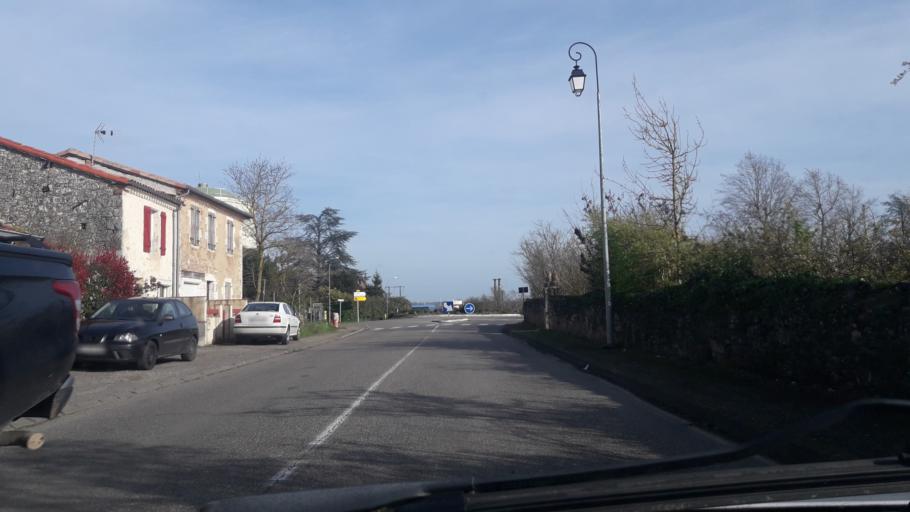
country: FR
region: Midi-Pyrenees
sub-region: Departement du Gers
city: Gimont
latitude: 43.7280
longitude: 0.8839
